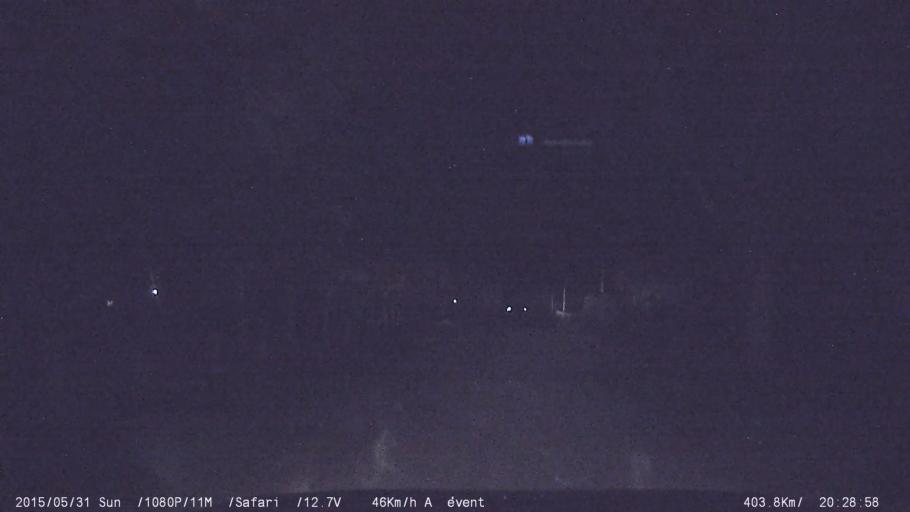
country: IN
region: Karnataka
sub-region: Mandya
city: Malavalli
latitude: 12.4530
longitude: 77.2313
